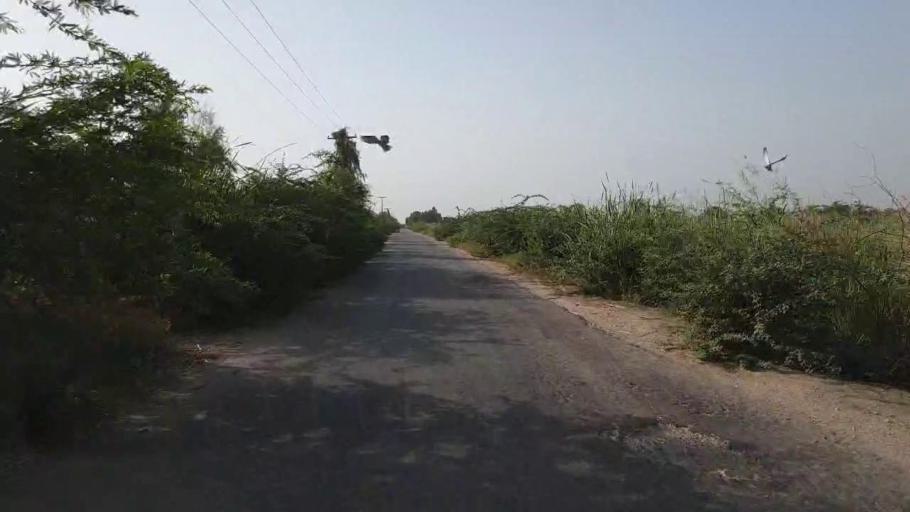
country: PK
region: Sindh
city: Jam Sahib
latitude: 26.4023
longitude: 68.8777
